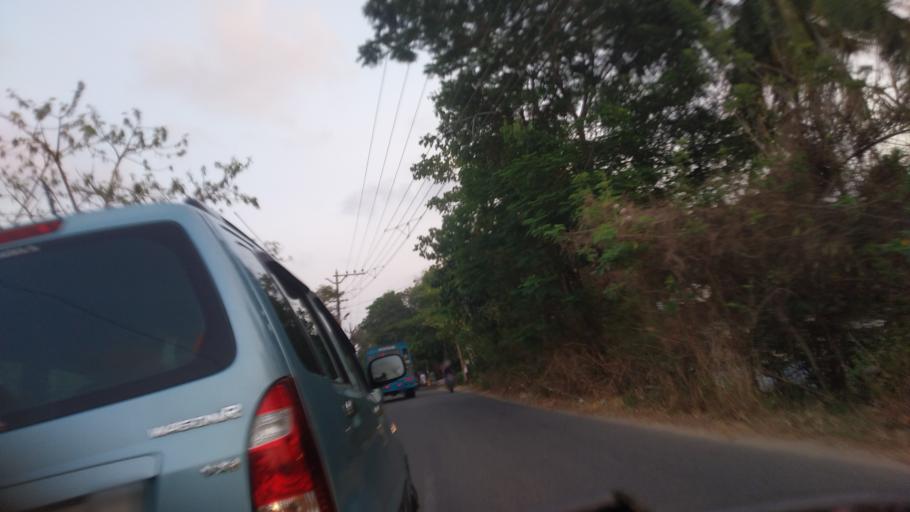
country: IN
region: Kerala
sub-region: Thrissur District
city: Kodungallur
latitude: 10.2160
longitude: 76.1606
